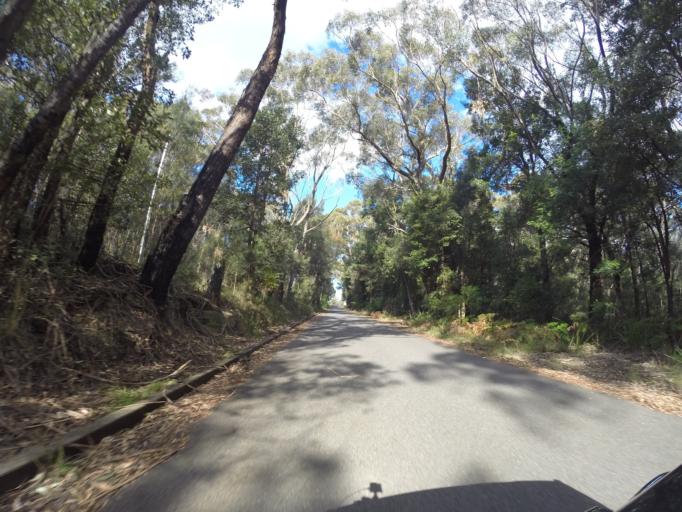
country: AU
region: New South Wales
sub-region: Wollongong
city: Mount Keira
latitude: -34.4011
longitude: 150.8558
